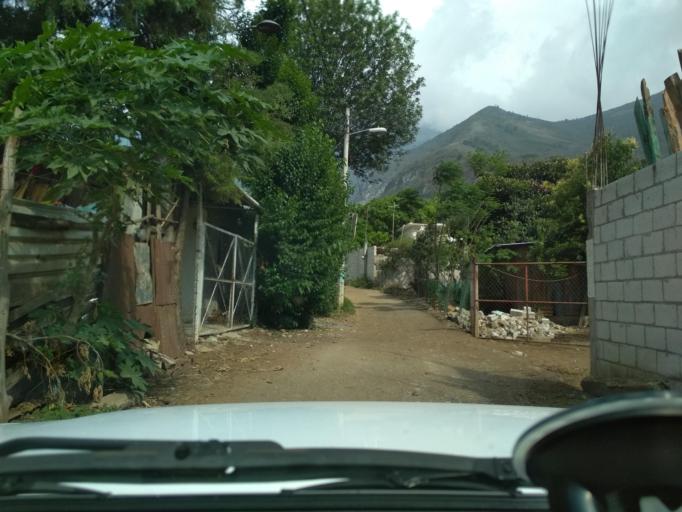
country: MX
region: Veracruz
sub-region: Nogales
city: Taza de Agua Ojo Zarco
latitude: 18.7787
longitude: -97.2040
